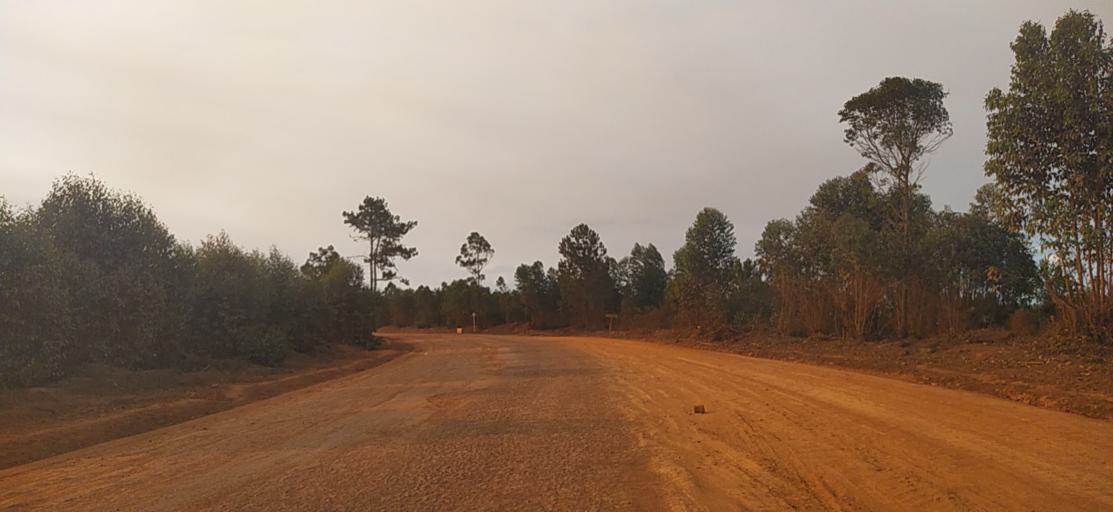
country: MG
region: Alaotra Mangoro
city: Moramanga
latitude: -18.5759
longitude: 48.2700
